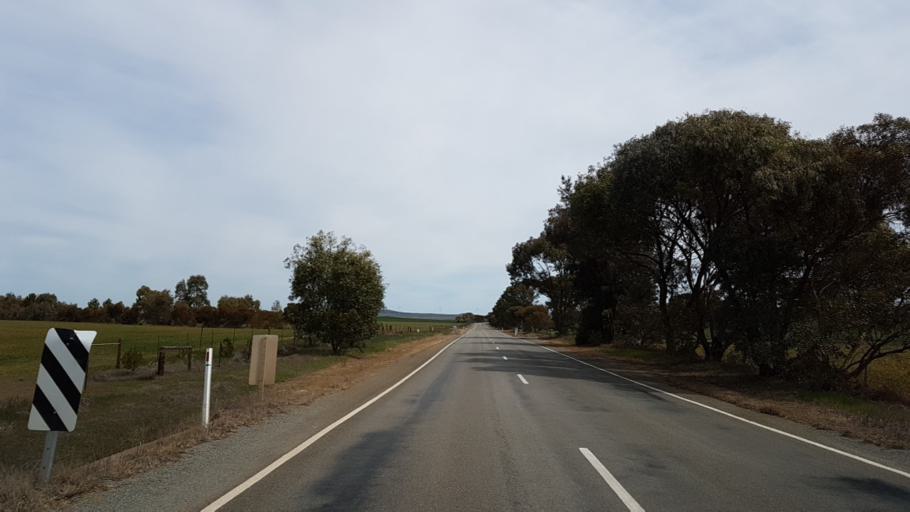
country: AU
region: South Australia
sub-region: Northern Areas
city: Jamestown
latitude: -33.0321
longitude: 138.6593
